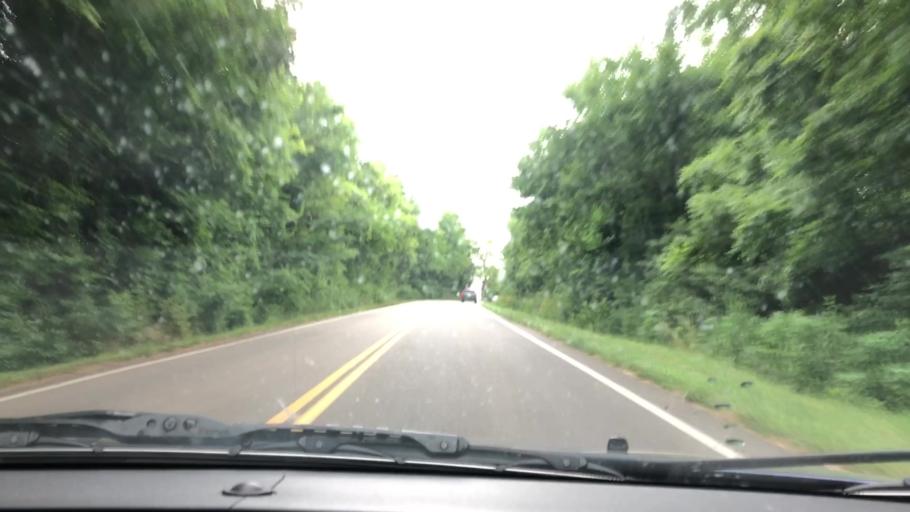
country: US
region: Tennessee
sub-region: Maury County
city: Columbia
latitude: 35.6854
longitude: -87.0109
